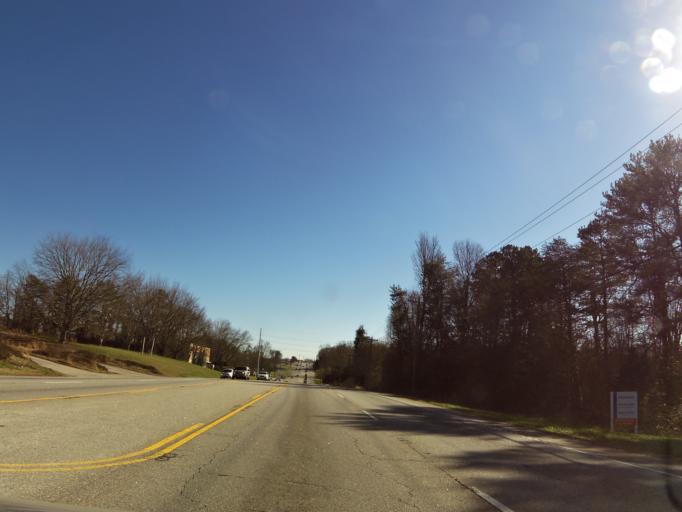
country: US
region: South Carolina
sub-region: Greenville County
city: Sans Souci
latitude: 34.8978
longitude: -82.4128
